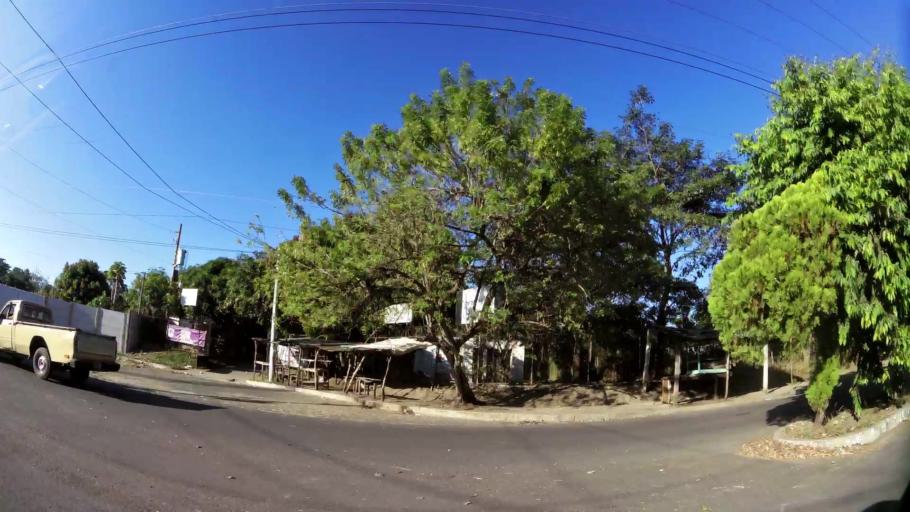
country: SV
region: La Libertad
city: Santa Tecla
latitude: 13.7353
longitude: -89.3581
